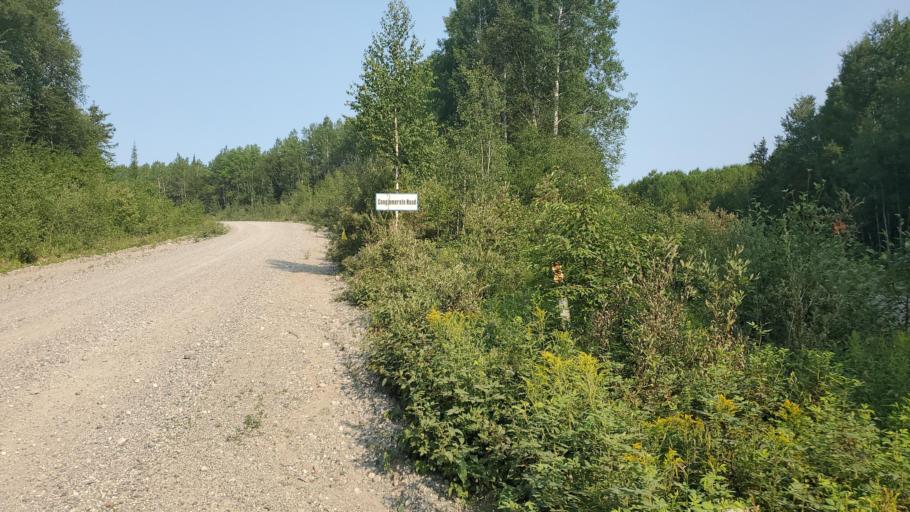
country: CA
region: Ontario
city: Greenstone
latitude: 49.9831
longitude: -87.6855
